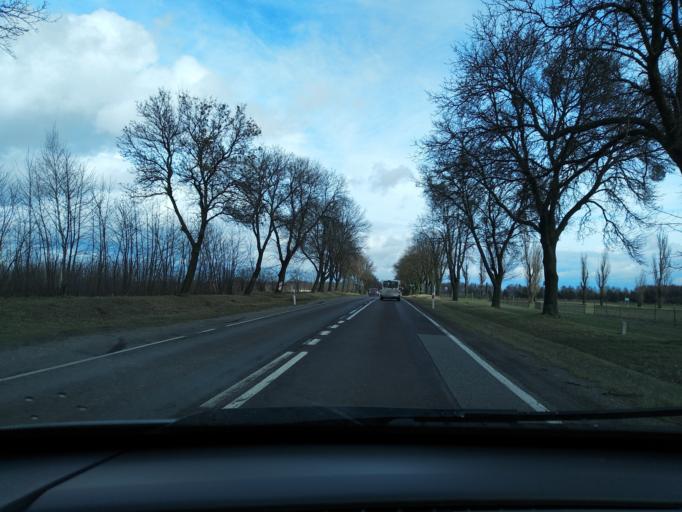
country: PL
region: Lodz Voivodeship
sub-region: Powiat zgierski
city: Zgierz
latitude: 51.8646
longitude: 19.5084
